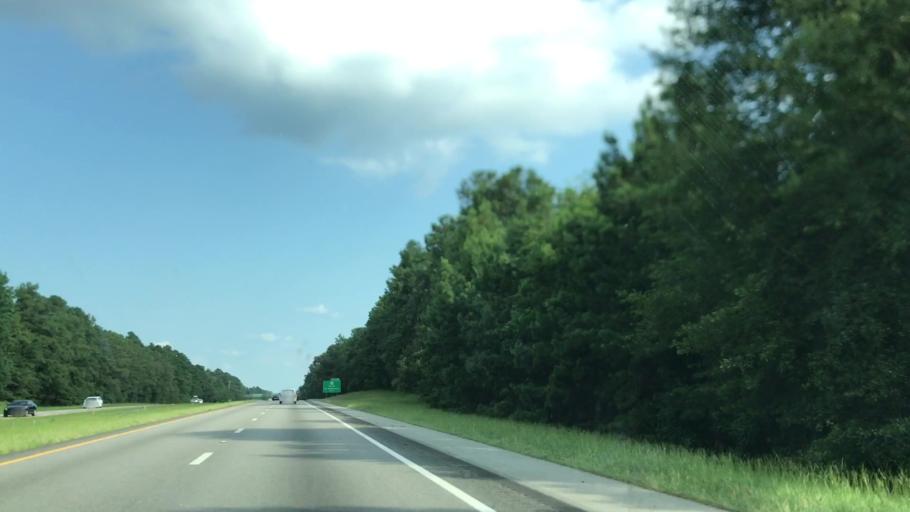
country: US
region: South Carolina
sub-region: Calhoun County
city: Oak Grove
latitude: 33.6869
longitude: -80.9079
